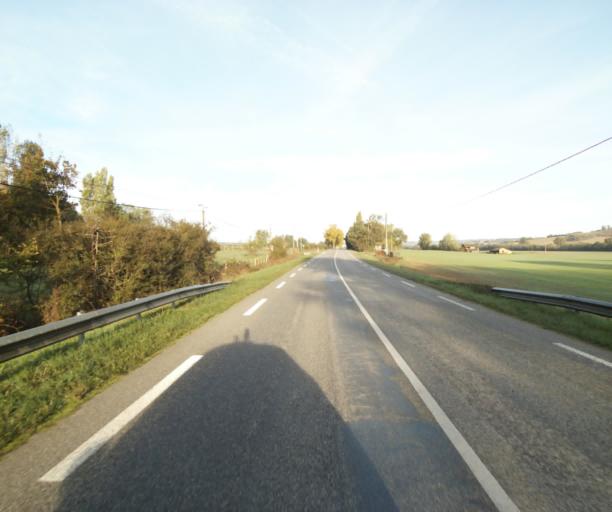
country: FR
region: Midi-Pyrenees
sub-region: Departement du Tarn-et-Garonne
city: Saint-Nauphary
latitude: 43.9492
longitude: 1.4514
